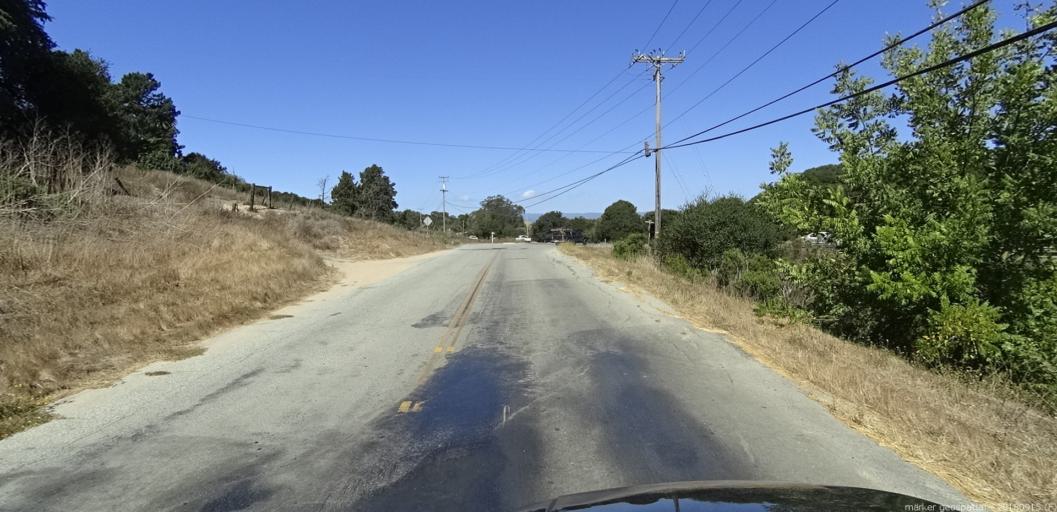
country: US
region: California
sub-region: Monterey County
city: Las Lomas
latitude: 36.8748
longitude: -121.7461
